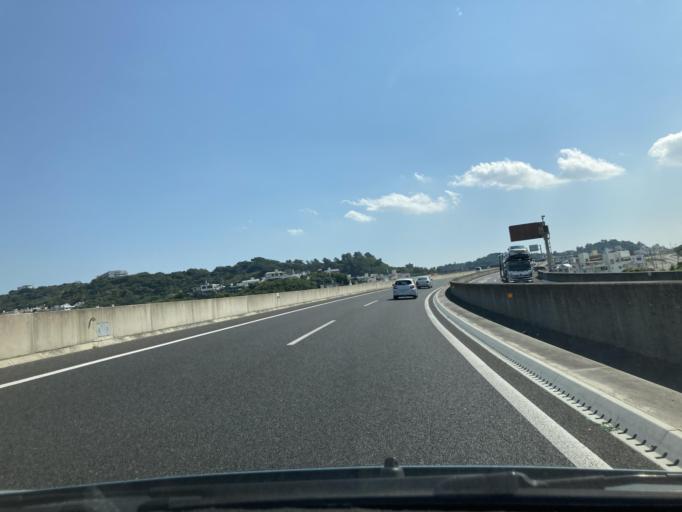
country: JP
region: Okinawa
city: Tomigusuku
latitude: 26.1748
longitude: 127.6746
